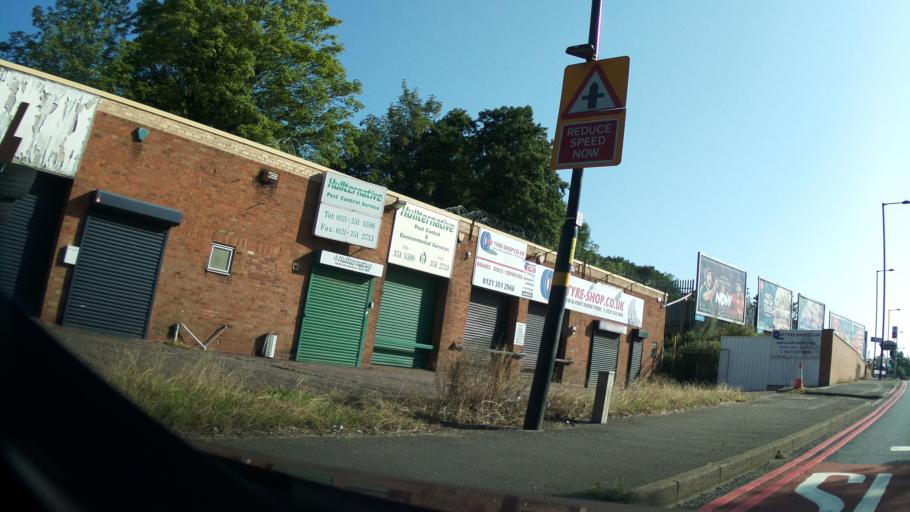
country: GB
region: England
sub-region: Warwickshire
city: Water Orton
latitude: 52.5267
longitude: -1.7866
